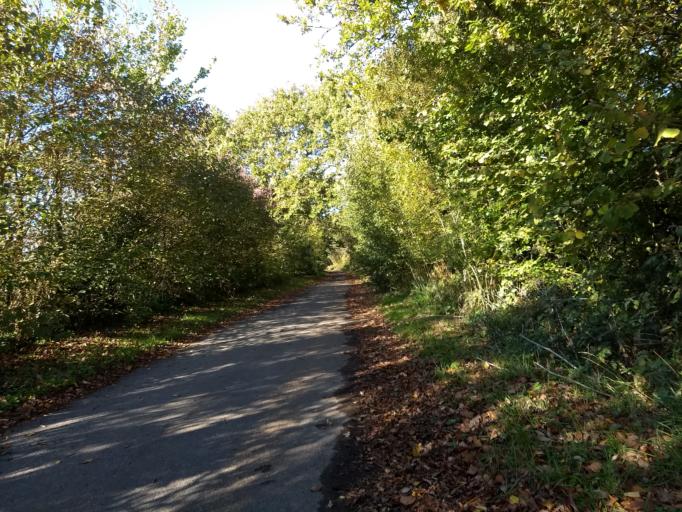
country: GB
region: England
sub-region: Isle of Wight
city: Newport
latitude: 50.6615
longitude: -1.2608
